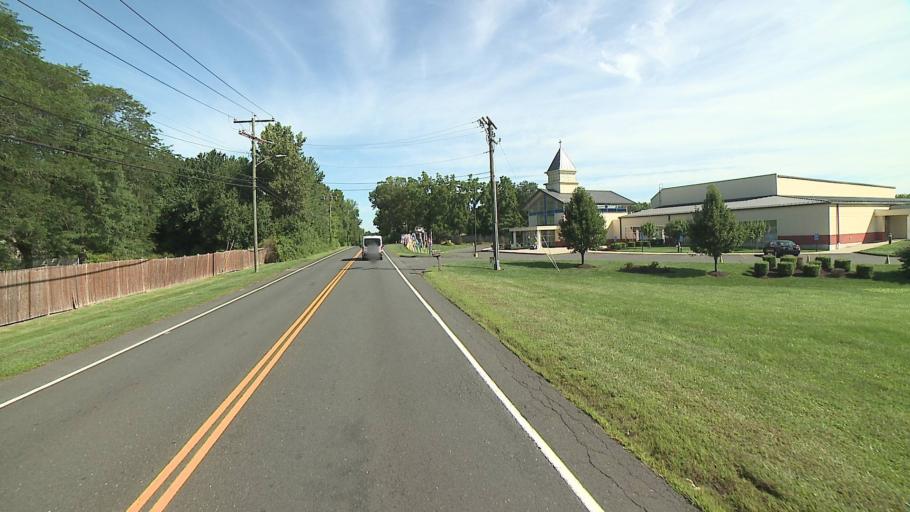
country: US
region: Connecticut
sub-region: Hartford County
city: Blue Hills
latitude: 41.8380
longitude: -72.6995
